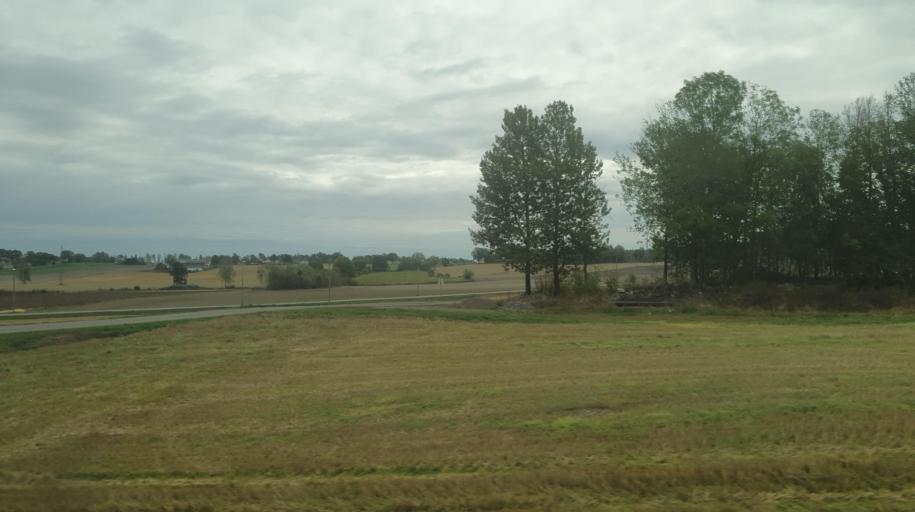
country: NO
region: Vestfold
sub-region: Tonsberg
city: Barkaker
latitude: 59.3455
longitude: 10.4183
